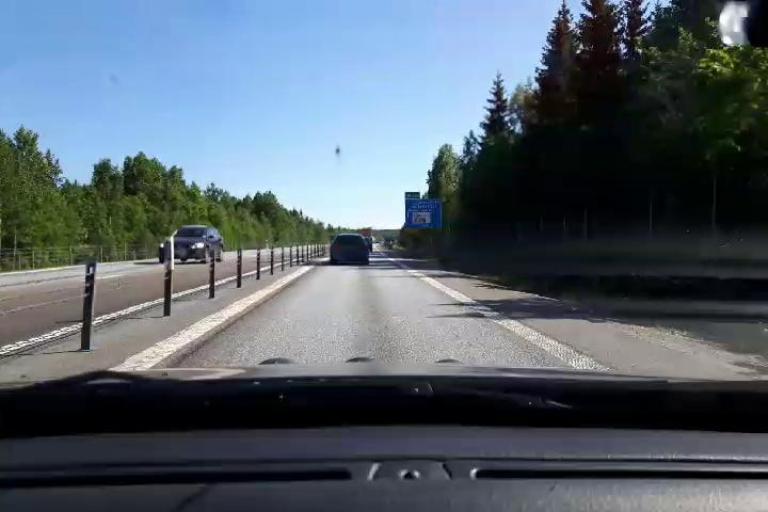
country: SE
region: Gaevleborg
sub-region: Gavle Kommun
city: Norrsundet
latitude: 60.9170
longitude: 17.0137
